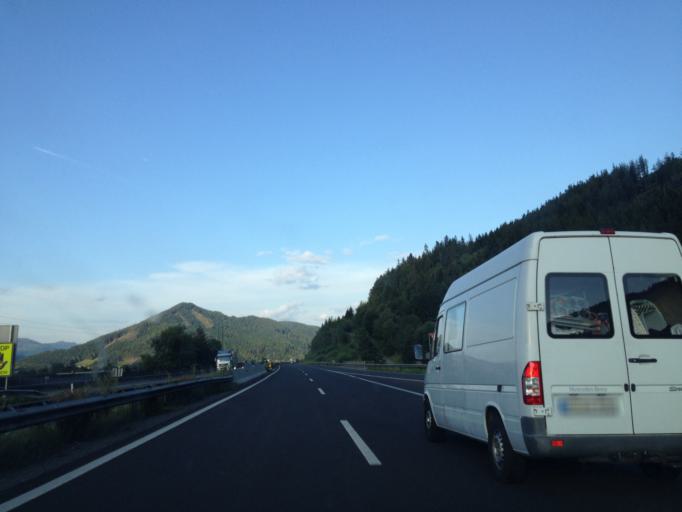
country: AT
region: Styria
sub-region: Politischer Bezirk Leoben
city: Kammern im Liesingtal
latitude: 47.3868
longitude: 14.9016
